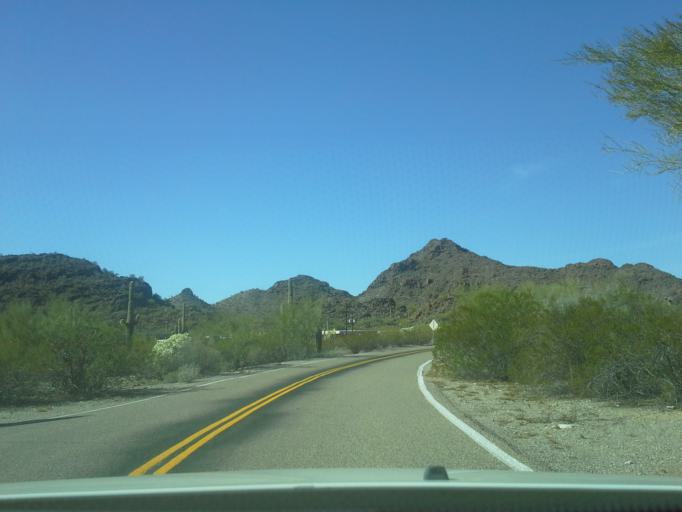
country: MX
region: Sonora
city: Sonoyta
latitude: 31.9543
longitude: -112.8028
